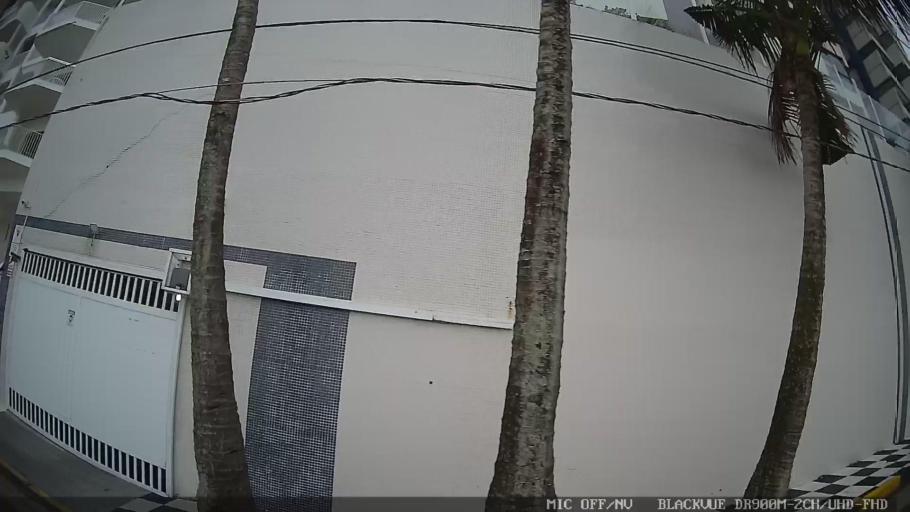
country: BR
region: Sao Paulo
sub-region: Guaruja
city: Guaruja
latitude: -23.9960
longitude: -46.2492
